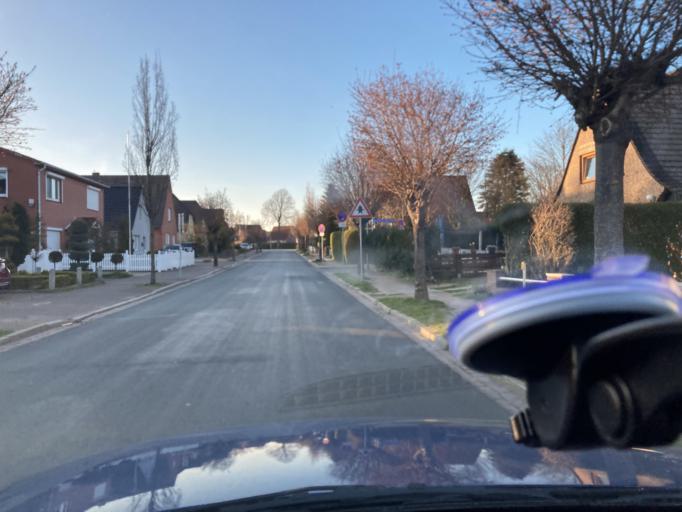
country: DE
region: Schleswig-Holstein
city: Wesseln
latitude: 54.1973
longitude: 9.0825
